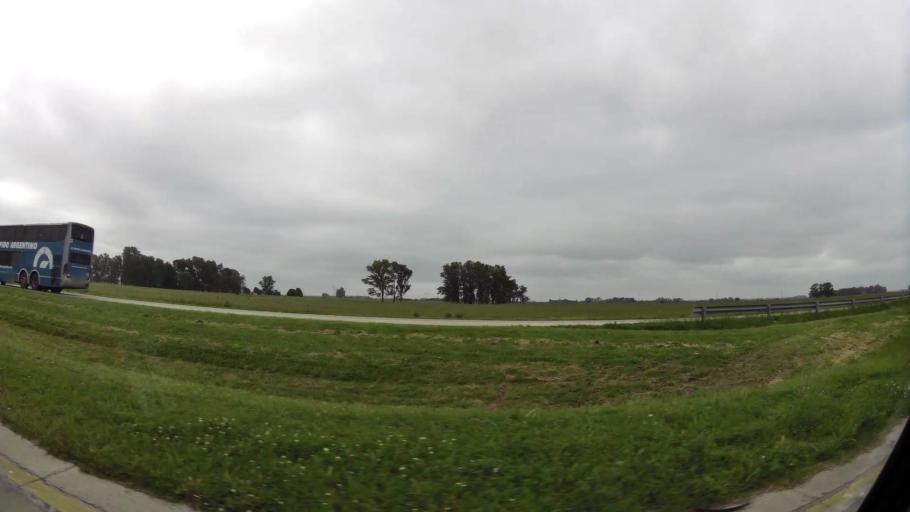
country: AR
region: Buenos Aires
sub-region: Partido de Brandsen
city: Brandsen
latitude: -35.0267
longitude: -58.2148
